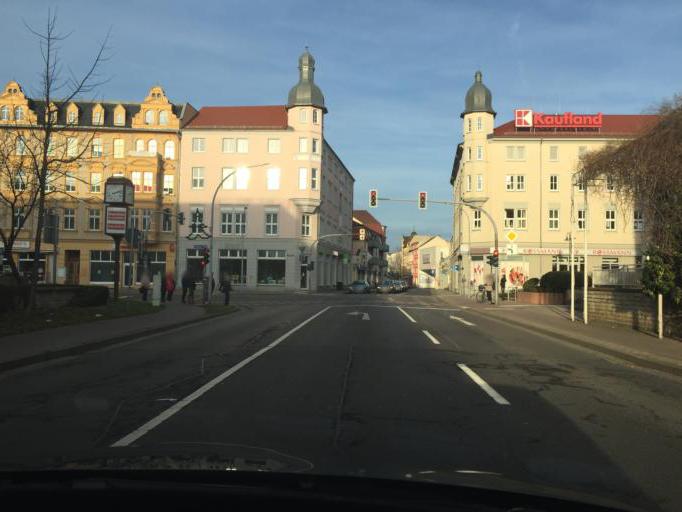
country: DE
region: Brandenburg
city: Forst
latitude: 51.7441
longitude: 14.6450
